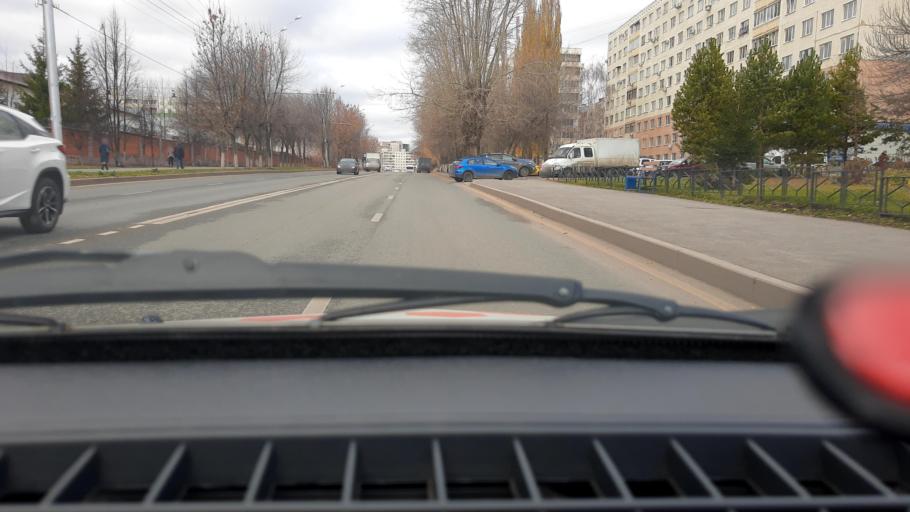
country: RU
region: Bashkortostan
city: Ufa
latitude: 54.6937
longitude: 56.0010
